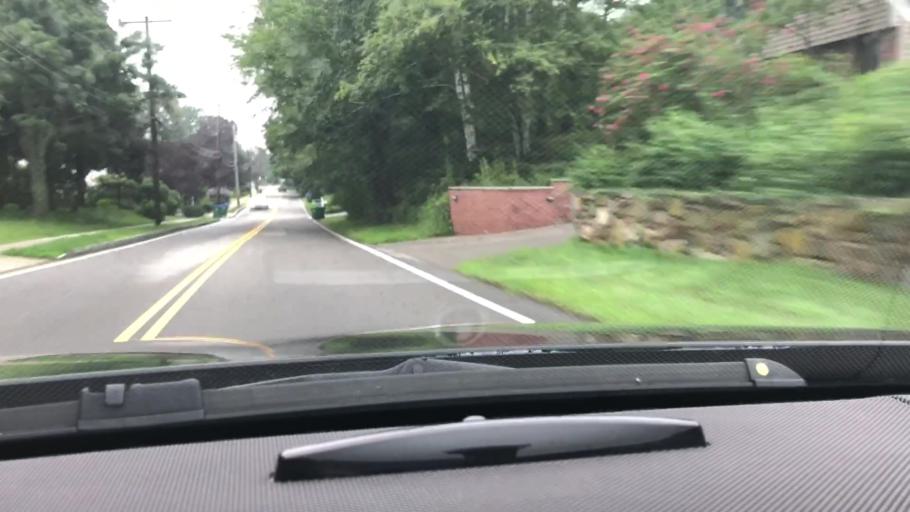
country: US
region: Massachusetts
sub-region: Norfolk County
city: Dedham
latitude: 42.2171
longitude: -71.1767
